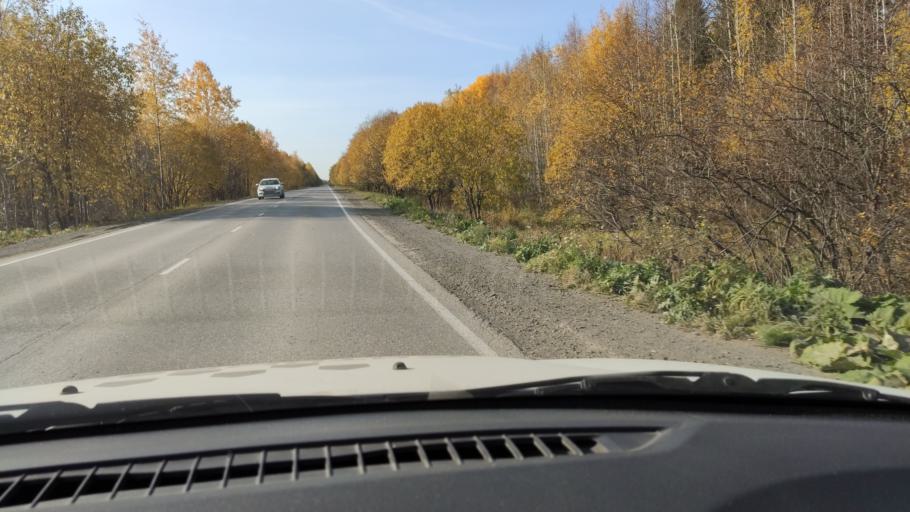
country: RU
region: Perm
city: Novyye Lyady
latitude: 58.0235
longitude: 56.6645
